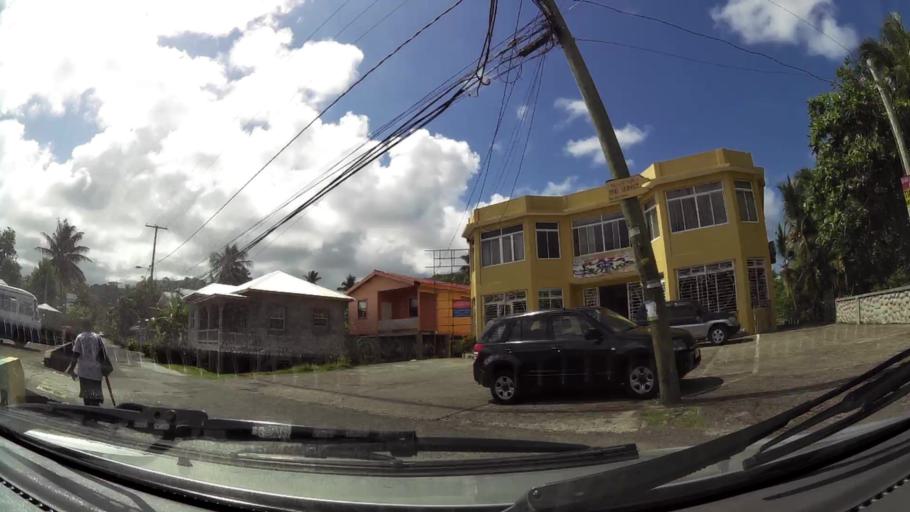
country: GD
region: Saint Patrick
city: Sauteurs
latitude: 12.2247
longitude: -61.6436
